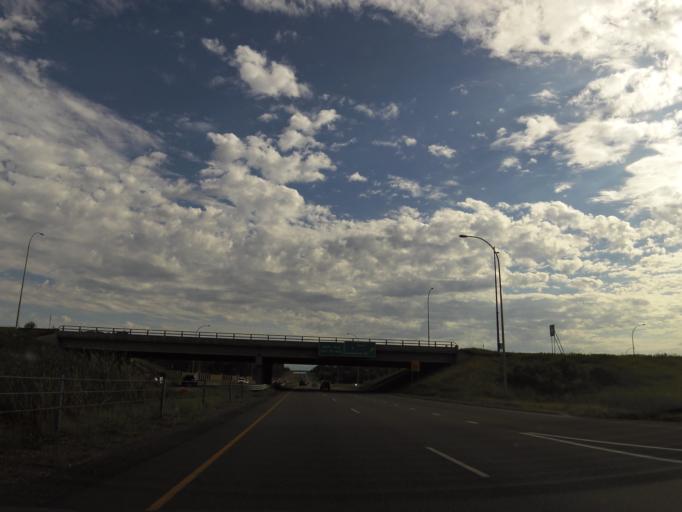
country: US
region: Minnesota
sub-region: Hennepin County
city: New Hope
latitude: 45.0342
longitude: -93.4009
